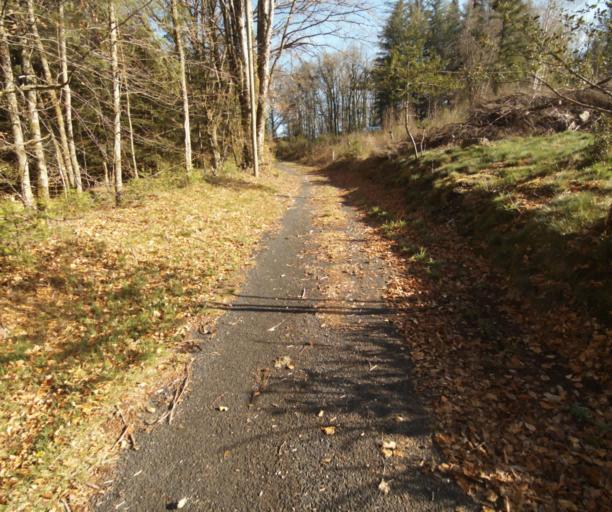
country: FR
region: Limousin
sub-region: Departement de la Correze
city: Correze
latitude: 45.3087
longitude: 1.8782
